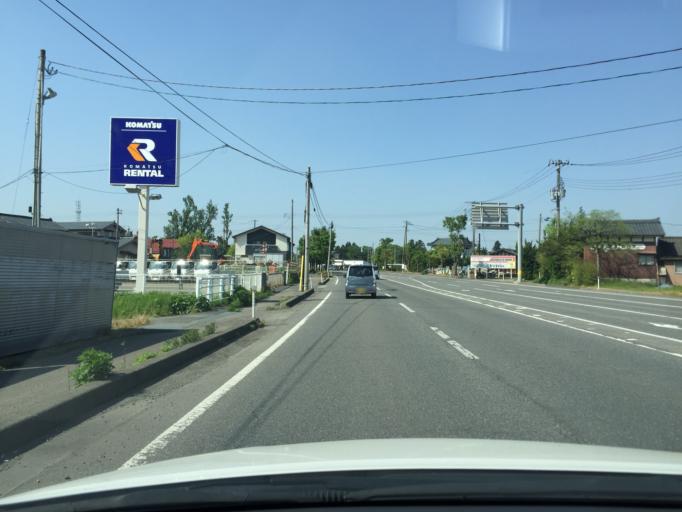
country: JP
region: Niigata
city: Gosen
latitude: 37.7660
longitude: 139.2364
